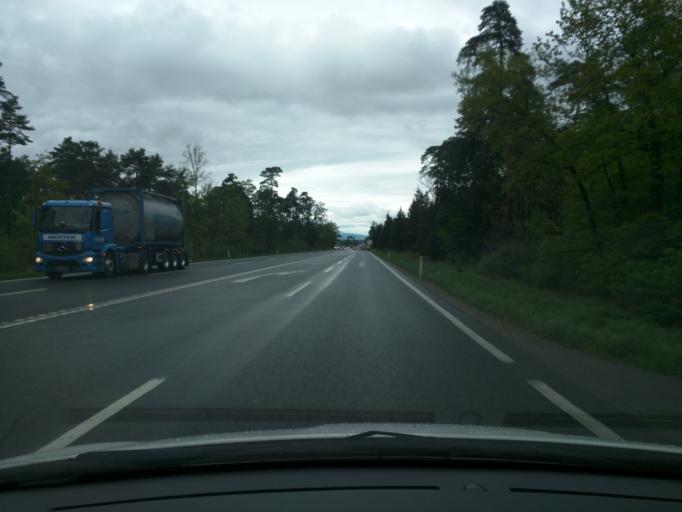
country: AT
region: Lower Austria
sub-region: Politischer Bezirk Amstetten
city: Winklarn
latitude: 48.0786
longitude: 14.7982
